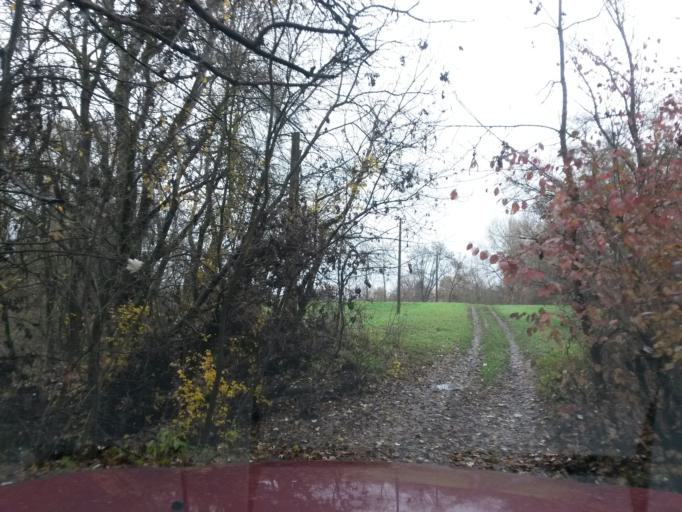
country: SK
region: Kosicky
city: Michalovce
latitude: 48.5591
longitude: 21.9501
